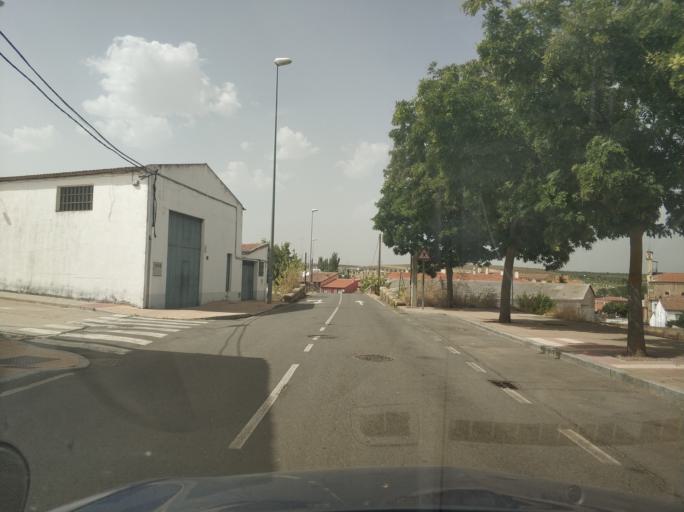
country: ES
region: Castille and Leon
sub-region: Provincia de Salamanca
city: Aldeatejada
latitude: 40.9529
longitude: -5.6942
